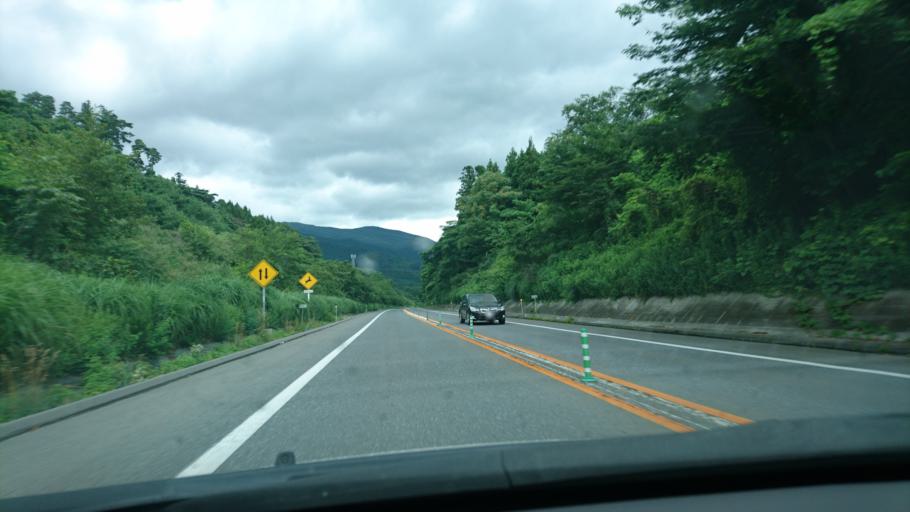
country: JP
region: Iwate
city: Ofunato
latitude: 39.1177
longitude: 141.7148
